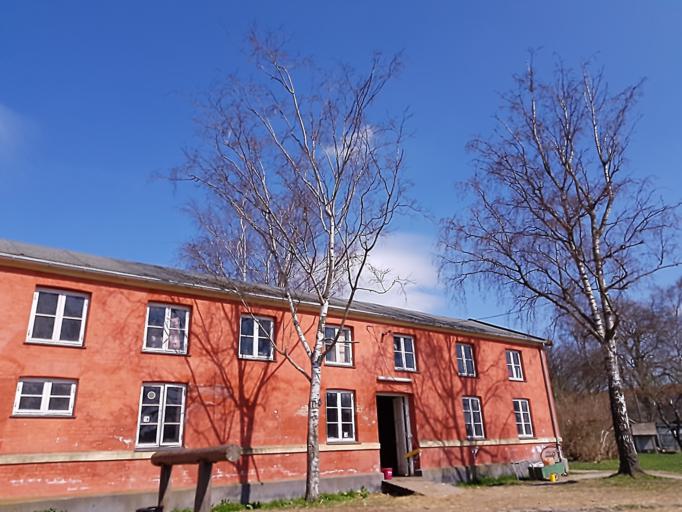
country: DK
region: Capital Region
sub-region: Frederiksberg Kommune
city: Frederiksberg
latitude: 55.6461
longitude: 12.5297
